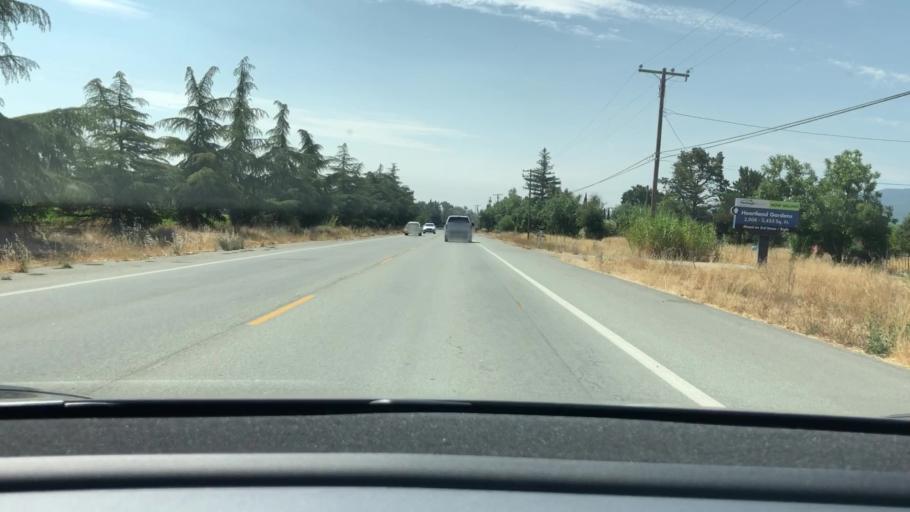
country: US
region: California
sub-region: Santa Clara County
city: San Martin
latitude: 37.0459
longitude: -121.6013
